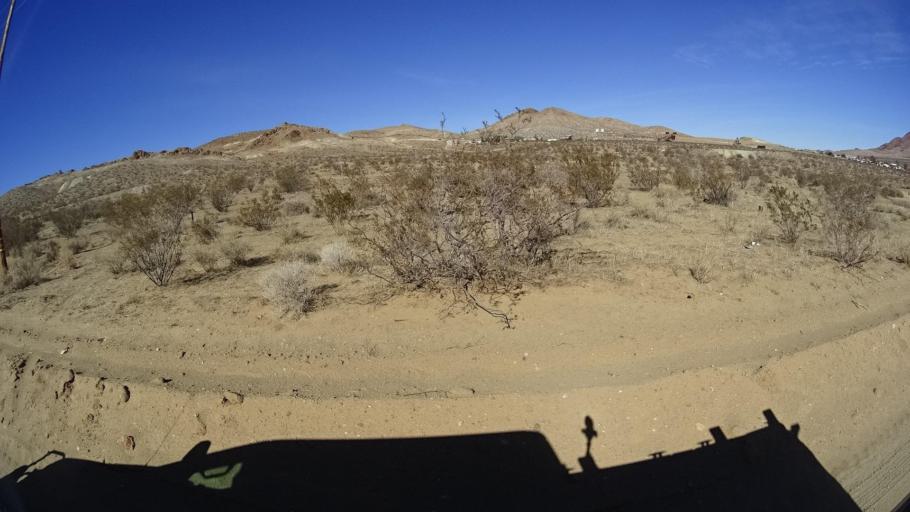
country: US
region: California
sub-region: Kern County
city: Ridgecrest
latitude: 35.3461
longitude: -117.6249
